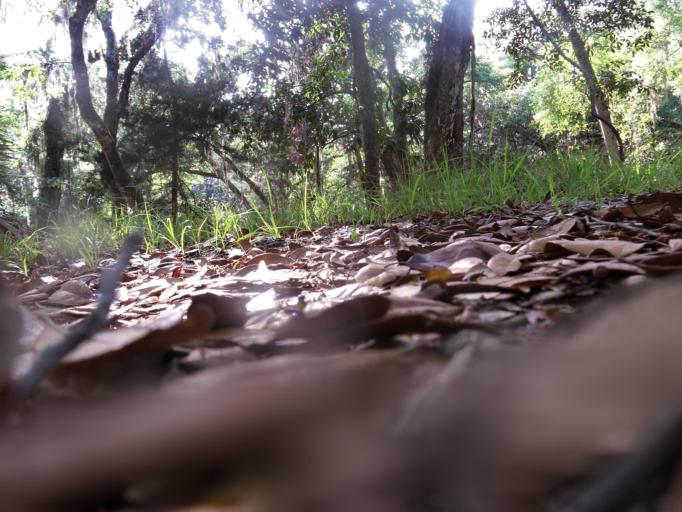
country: US
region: Florida
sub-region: Saint Johns County
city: Villano Beach
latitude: 30.0144
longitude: -81.3396
